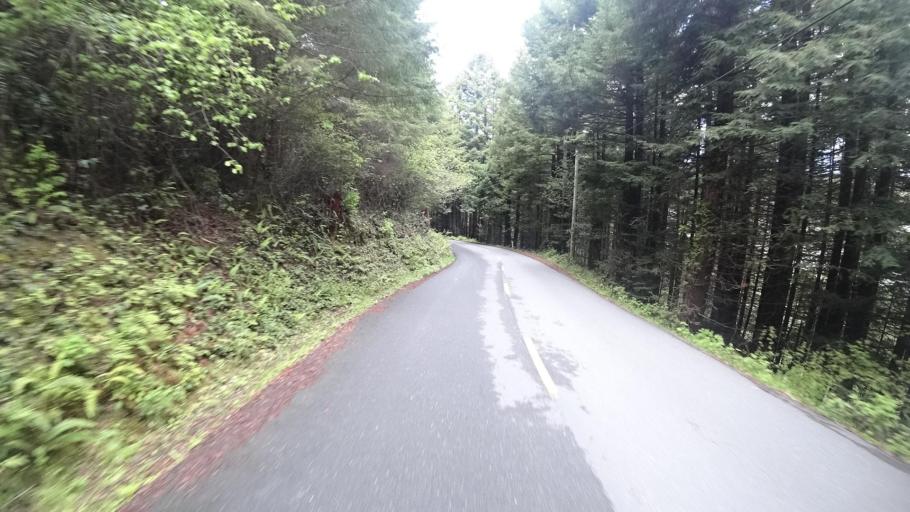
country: US
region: California
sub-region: Humboldt County
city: Blue Lake
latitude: 40.8703
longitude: -123.9561
